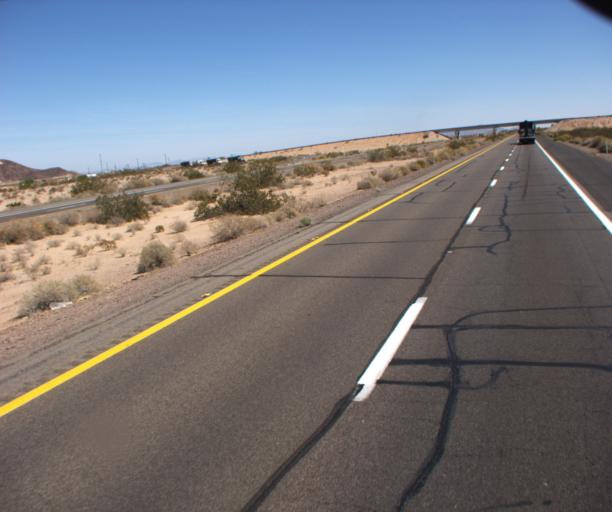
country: US
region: Arizona
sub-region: Yuma County
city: Wellton
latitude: 32.6805
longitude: -114.0262
